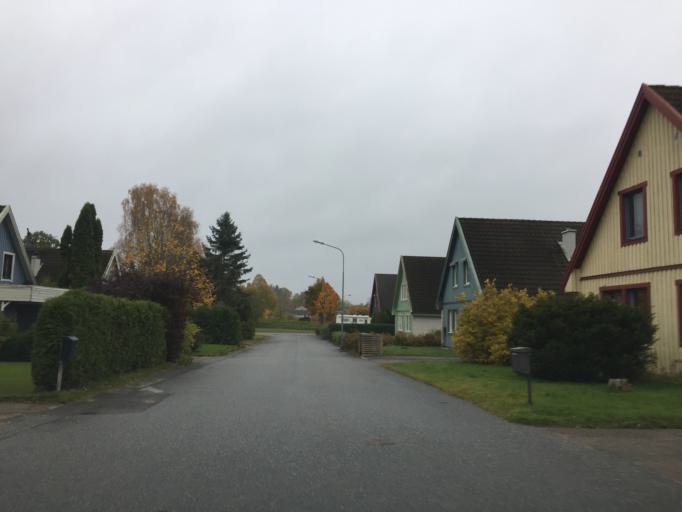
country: SE
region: Vaestra Goetaland
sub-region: Trollhattan
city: Sjuntorp
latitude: 58.1602
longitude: 12.3090
